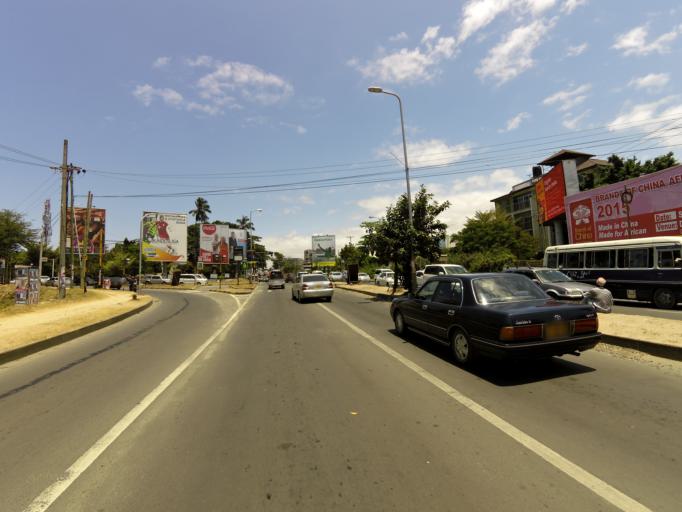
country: TZ
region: Dar es Salaam
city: Dar es Salaam
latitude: -6.7981
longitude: 39.2822
